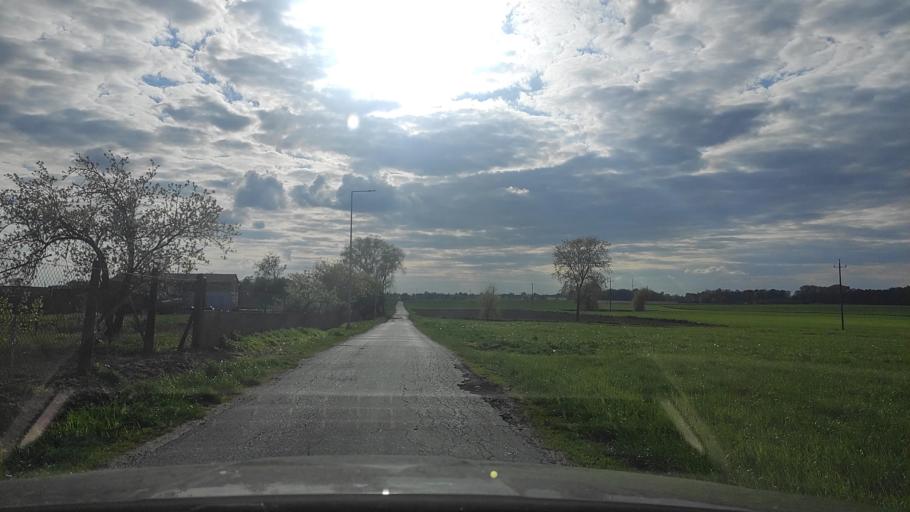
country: PL
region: Greater Poland Voivodeship
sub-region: Powiat poznanski
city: Kostrzyn
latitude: 52.3980
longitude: 17.1908
